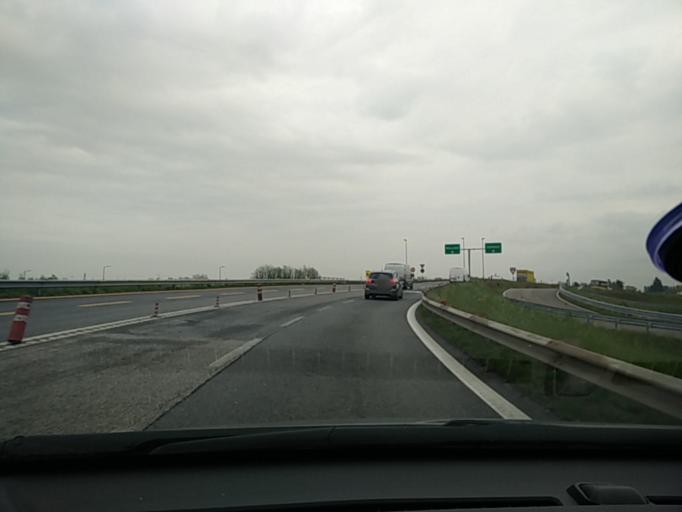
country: IT
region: Veneto
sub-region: Provincia di Treviso
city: Lancenigo-Villorba
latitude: 45.7225
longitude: 12.2842
